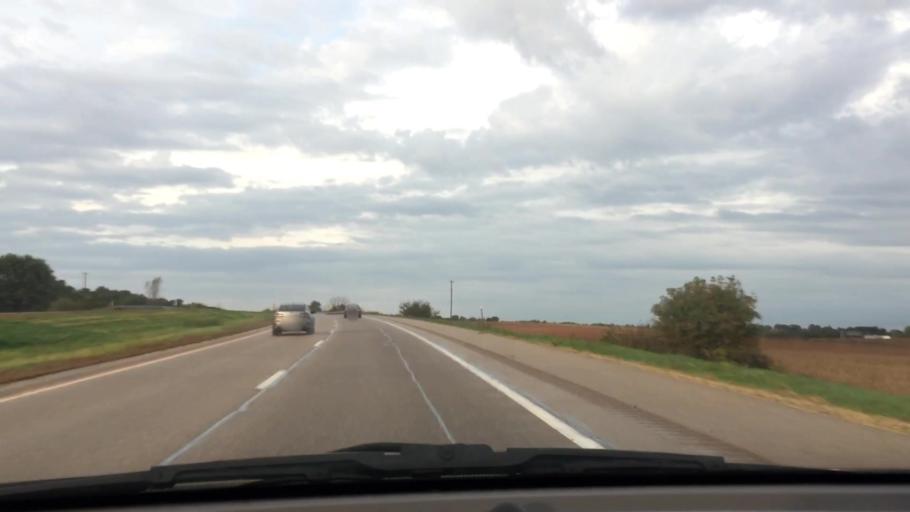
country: US
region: Wisconsin
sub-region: Rock County
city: Clinton
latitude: 42.5781
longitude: -88.7935
